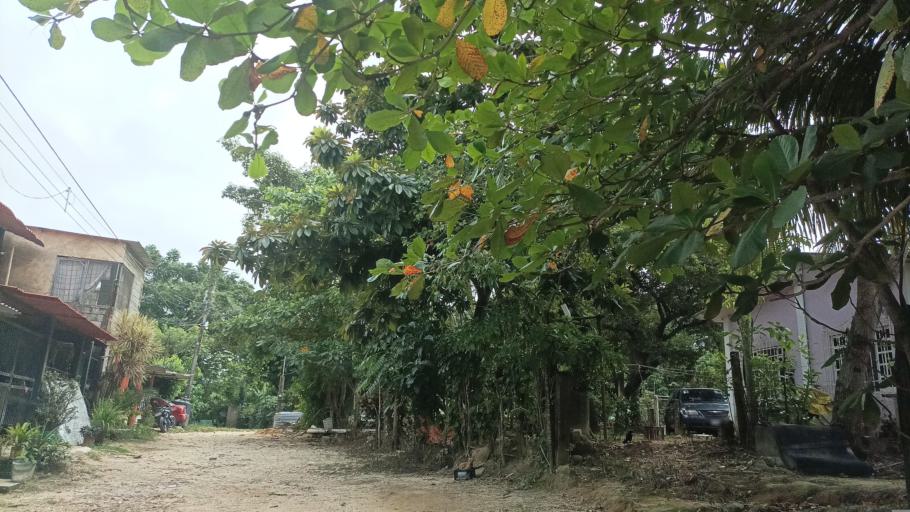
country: MX
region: Veracruz
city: Minatitlan
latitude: 18.0296
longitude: -94.5622
